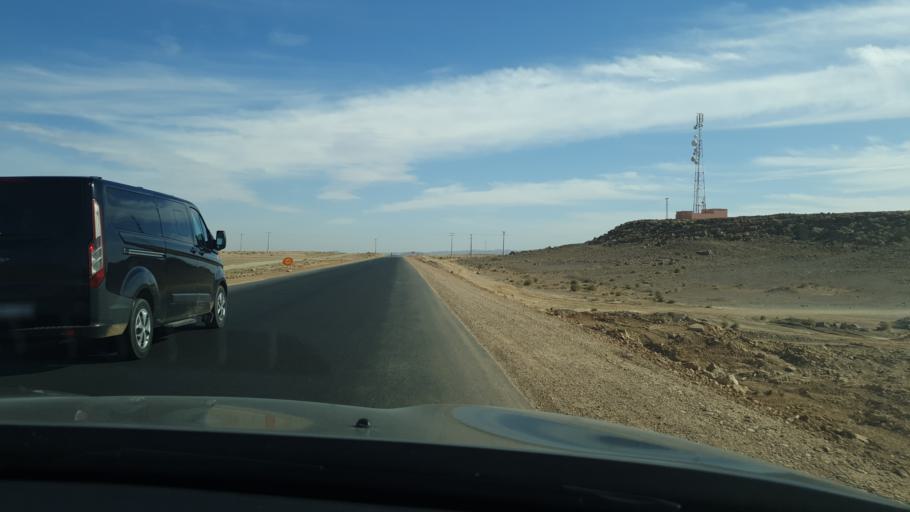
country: MA
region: Meknes-Tafilalet
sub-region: Errachidia
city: Goulmima
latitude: 31.4854
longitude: -5.1333
